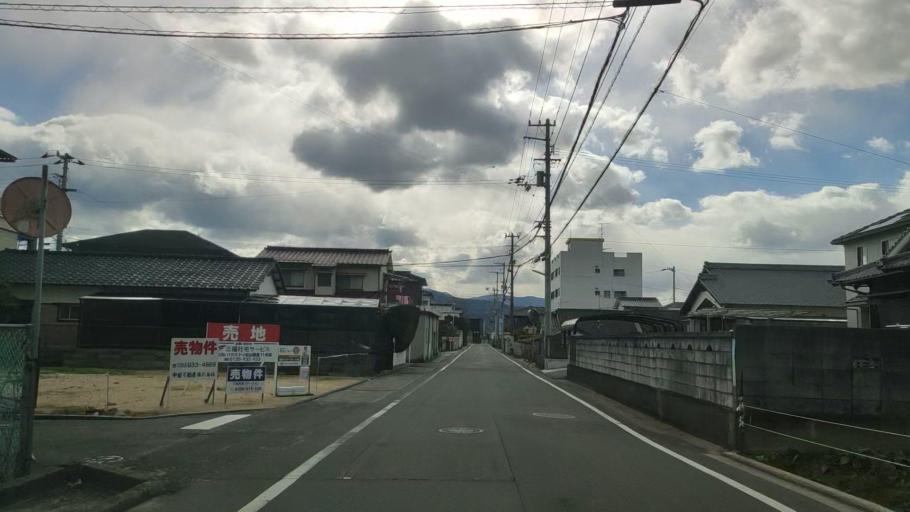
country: JP
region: Ehime
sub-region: Shikoku-chuo Shi
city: Matsuyama
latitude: 33.8112
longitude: 132.7525
